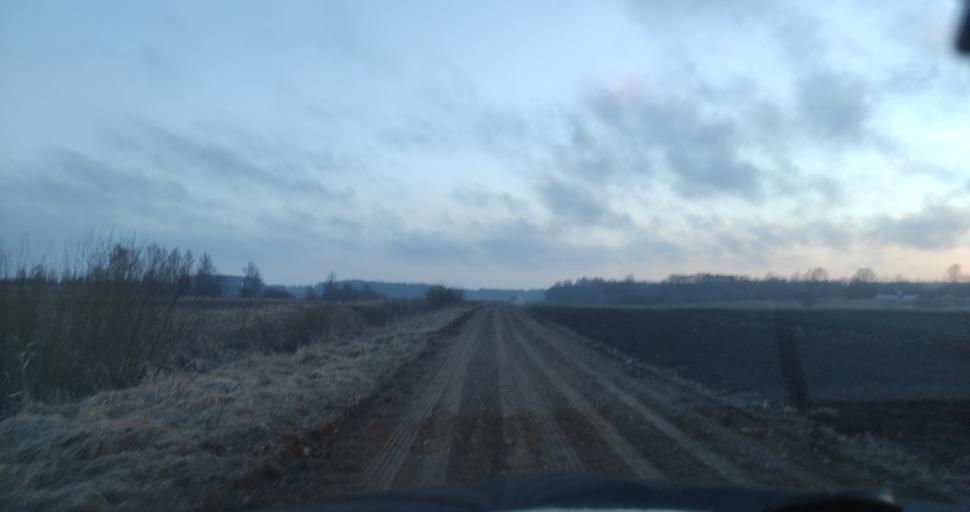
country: LV
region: Aizpute
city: Aizpute
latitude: 56.8142
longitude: 21.7864
